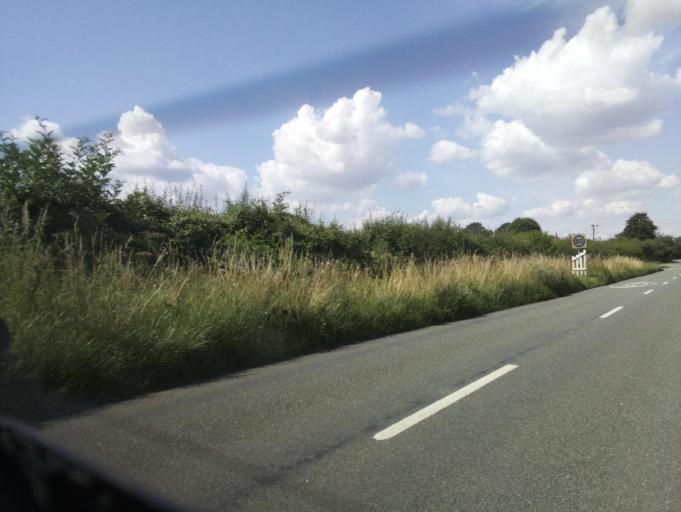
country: GB
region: England
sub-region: West Berkshire
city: Farnborough
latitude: 51.4950
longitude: -1.3669
